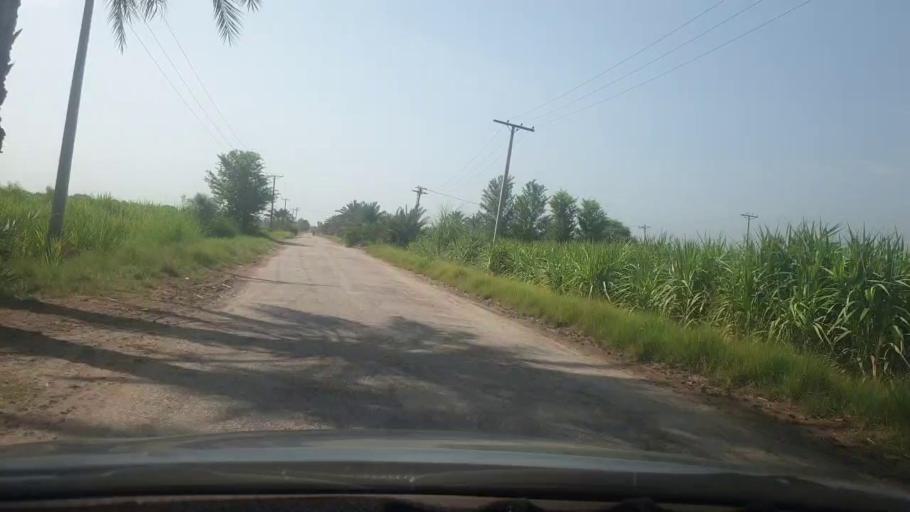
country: PK
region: Sindh
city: Gambat
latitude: 27.3250
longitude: 68.5529
